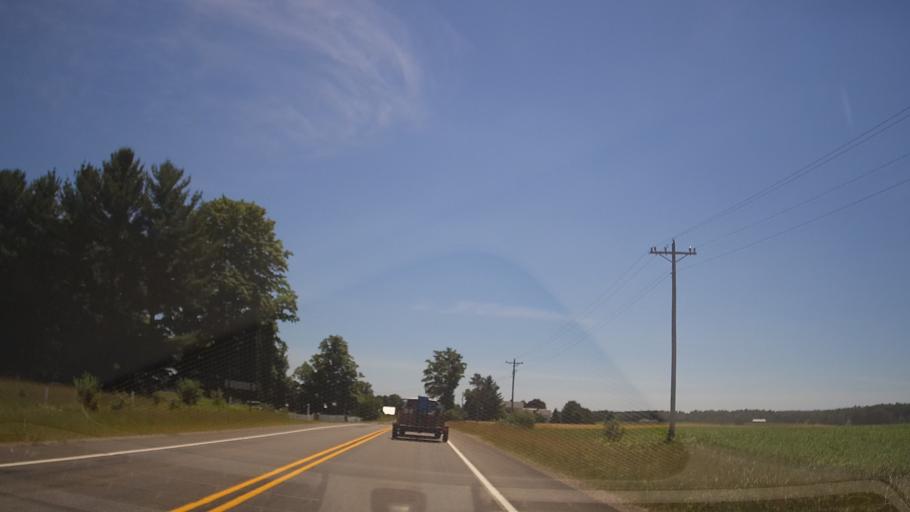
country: US
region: Michigan
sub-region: Grand Traverse County
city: Kingsley
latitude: 44.6101
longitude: -85.6965
